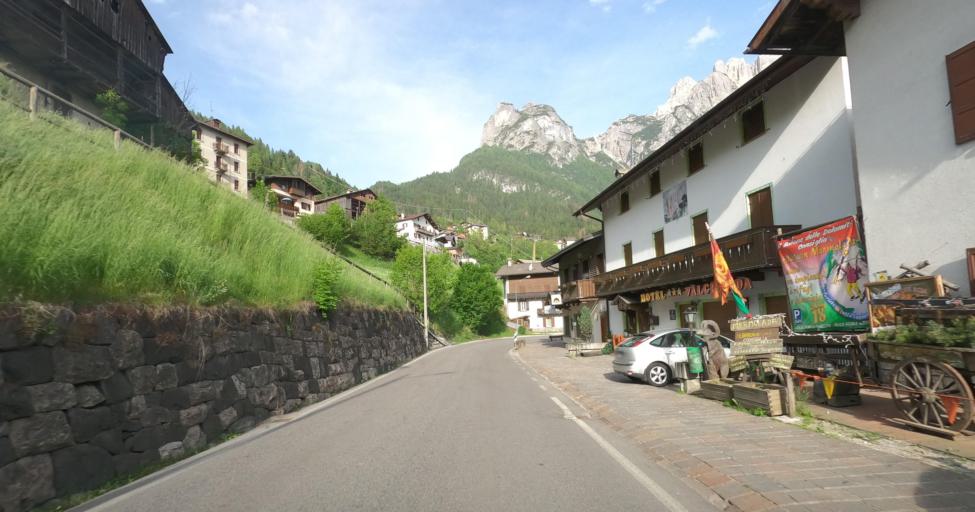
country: IT
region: Veneto
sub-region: Provincia di Belluno
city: Alleghe
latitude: 46.4060
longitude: 12.0225
